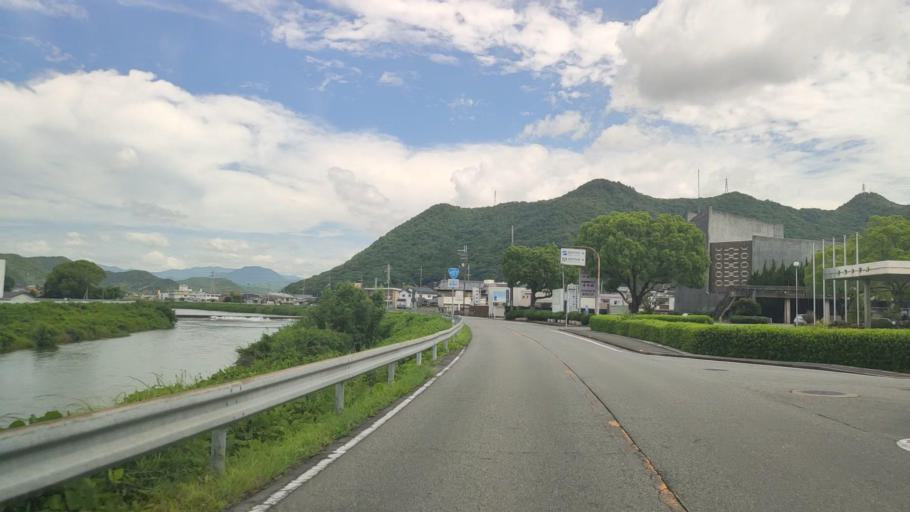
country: JP
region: Hyogo
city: Nishiwaki
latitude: 34.9929
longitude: 134.9687
